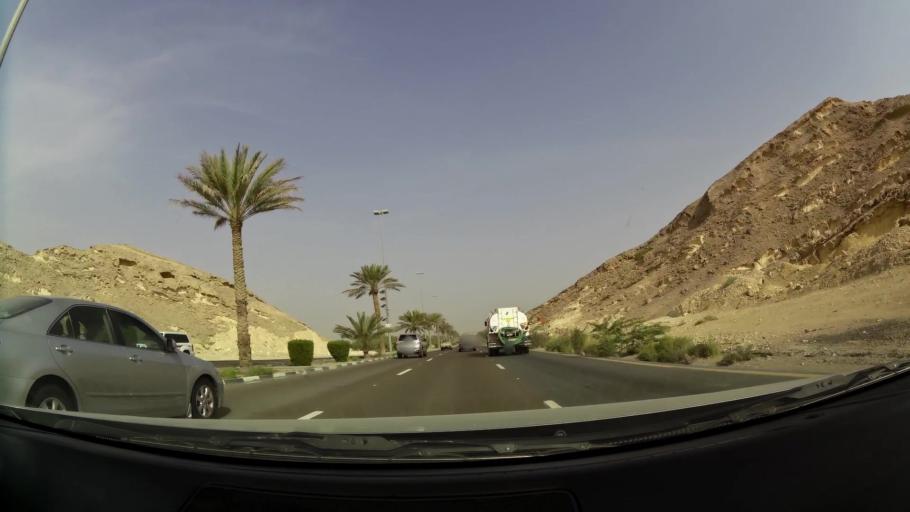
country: AE
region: Abu Dhabi
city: Al Ain
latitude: 24.1328
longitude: 55.7287
